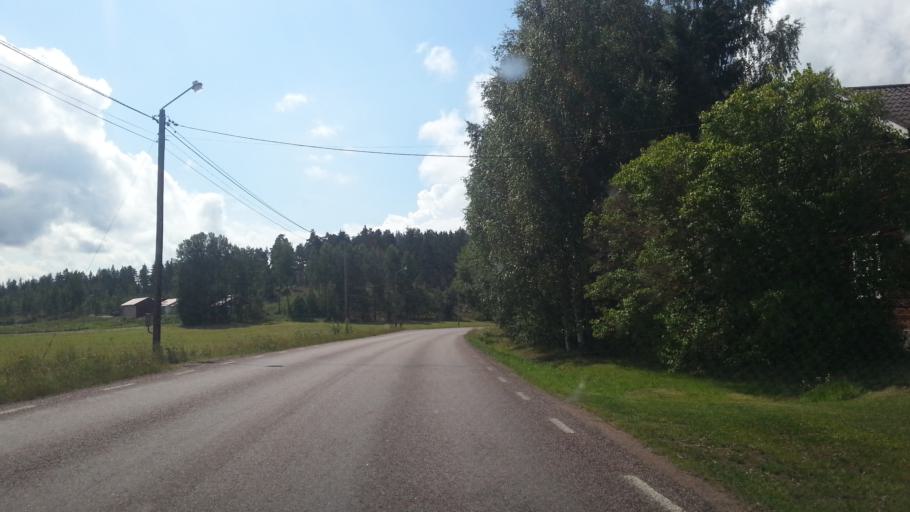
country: SE
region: Dalarna
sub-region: Faluns Kommun
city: Falun
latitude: 60.6376
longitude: 15.7760
